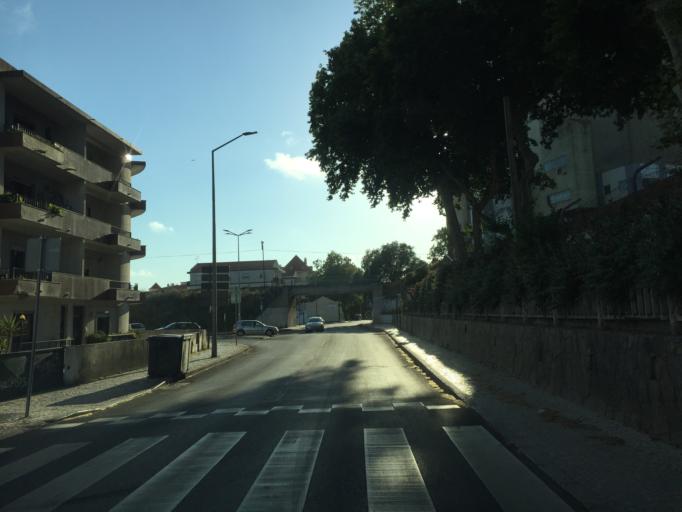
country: PT
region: Leiria
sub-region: Caldas da Rainha
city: Caldas da Rainha
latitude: 39.4019
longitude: -9.1380
